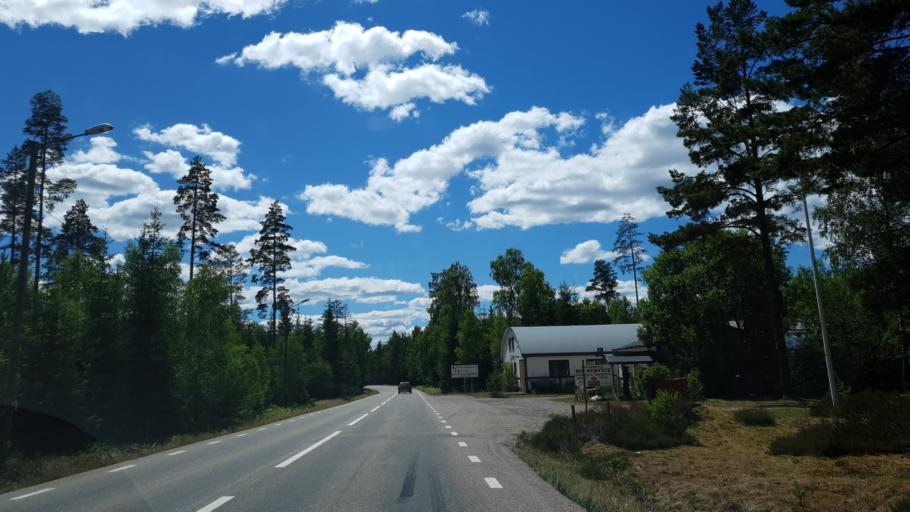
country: SE
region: Kronoberg
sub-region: Lessebo Kommun
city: Lessebo
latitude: 56.8201
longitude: 15.3798
